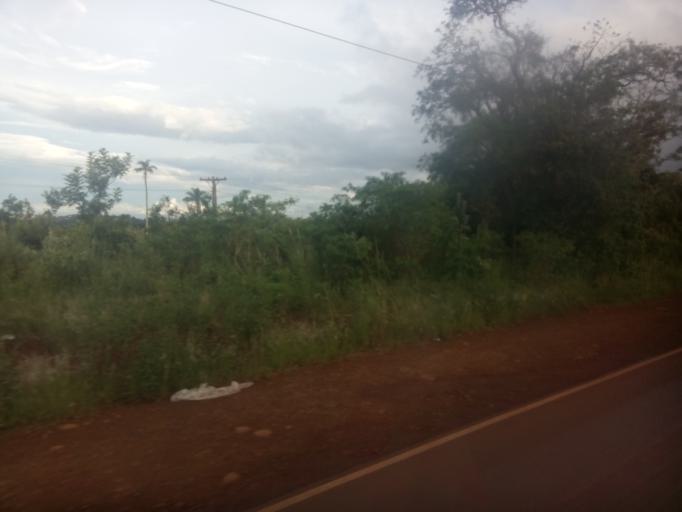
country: AR
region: Misiones
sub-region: Departamento de Obera
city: Obera
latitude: -27.5004
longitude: -55.1413
